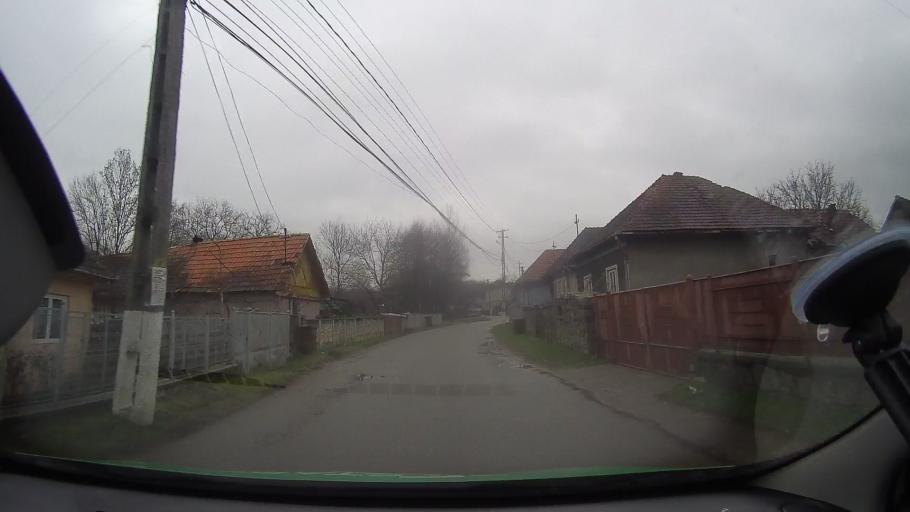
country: RO
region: Arad
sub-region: Comuna Halmagel
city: Halmagel
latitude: 46.2698
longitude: 22.6187
